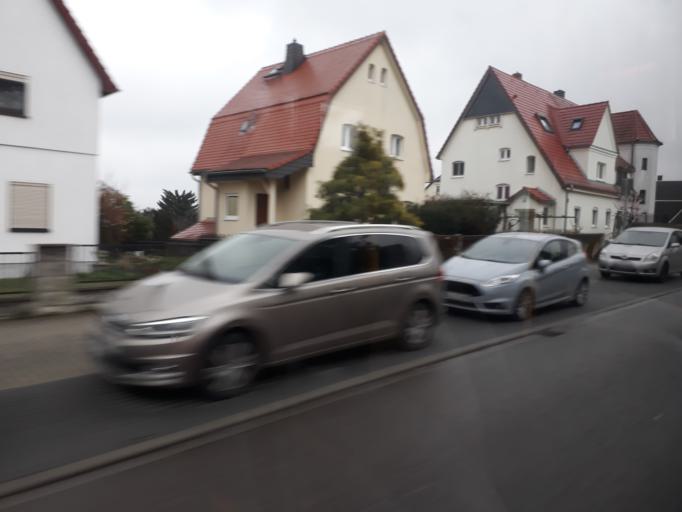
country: DE
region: Saxony
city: Kreischa
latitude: 50.9905
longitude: 13.8024
